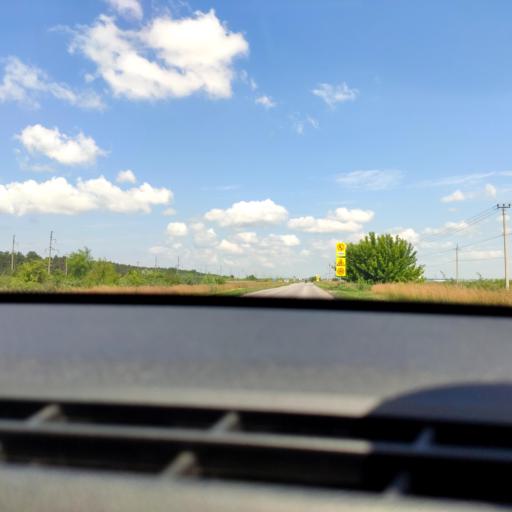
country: RU
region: Samara
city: Podstepki
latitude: 53.5291
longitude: 49.0849
